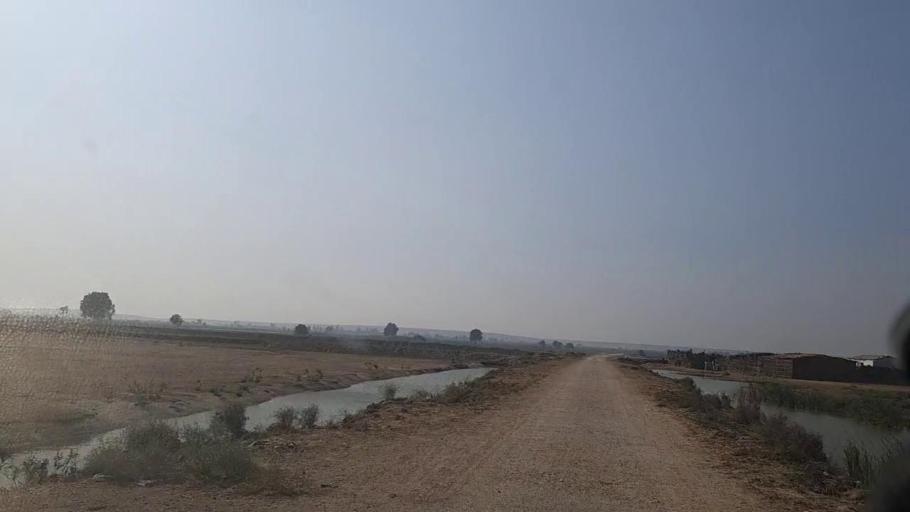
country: PK
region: Sindh
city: Thatta
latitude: 24.6155
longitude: 67.8894
